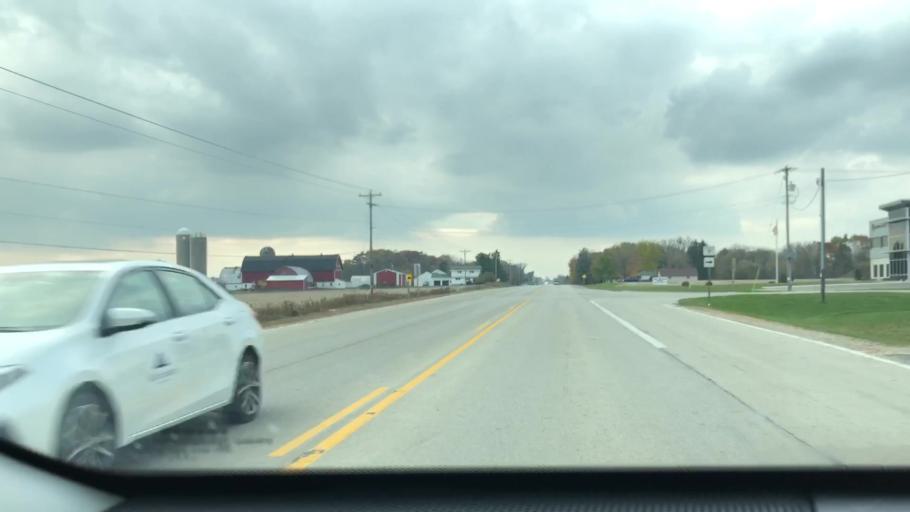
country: US
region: Wisconsin
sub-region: Outagamie County
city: Seymour
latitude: 44.5013
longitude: -88.2651
